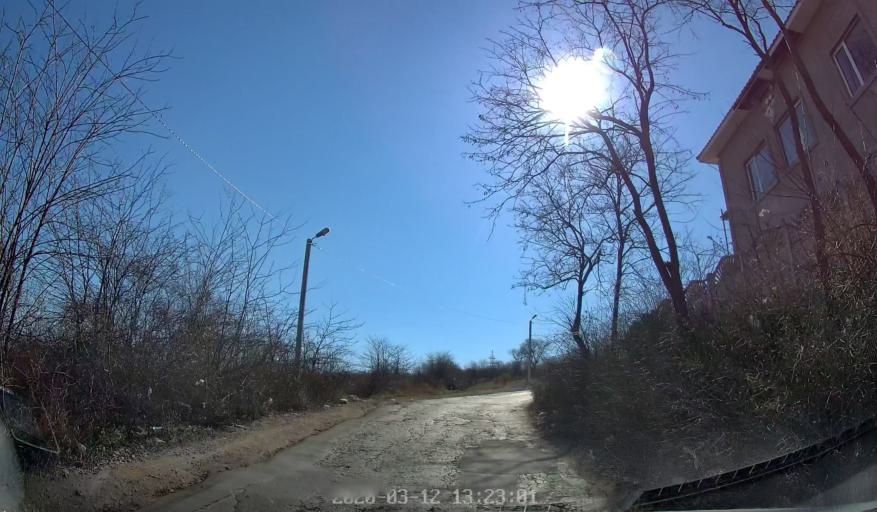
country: MD
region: Laloveni
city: Ialoveni
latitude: 46.9445
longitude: 28.8360
